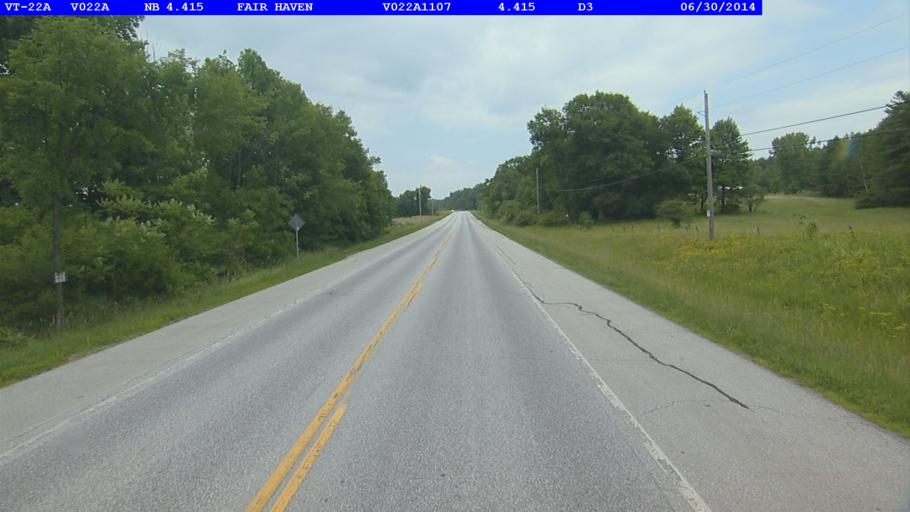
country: US
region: Vermont
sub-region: Rutland County
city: Fair Haven
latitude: 43.6283
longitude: -73.2969
